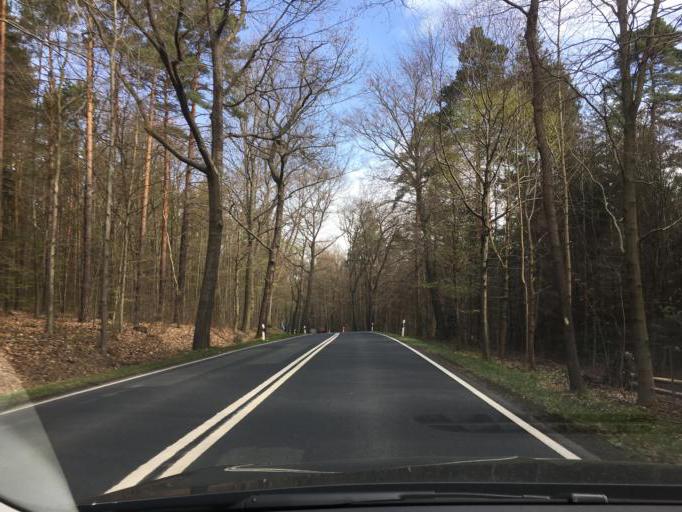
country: DE
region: Saxony
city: Ottendorf-Okrilla
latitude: 51.2232
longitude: 13.8434
